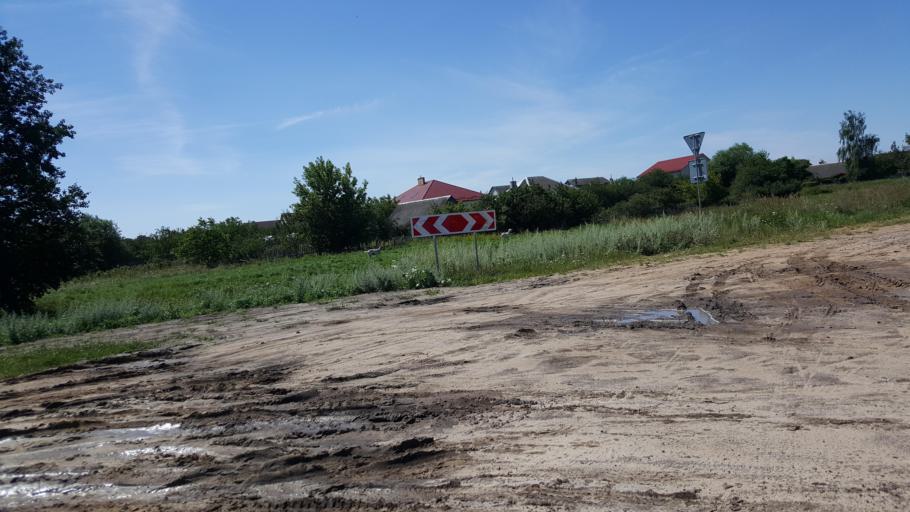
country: BY
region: Brest
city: Charnawchytsy
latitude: 52.2136
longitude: 23.7365
